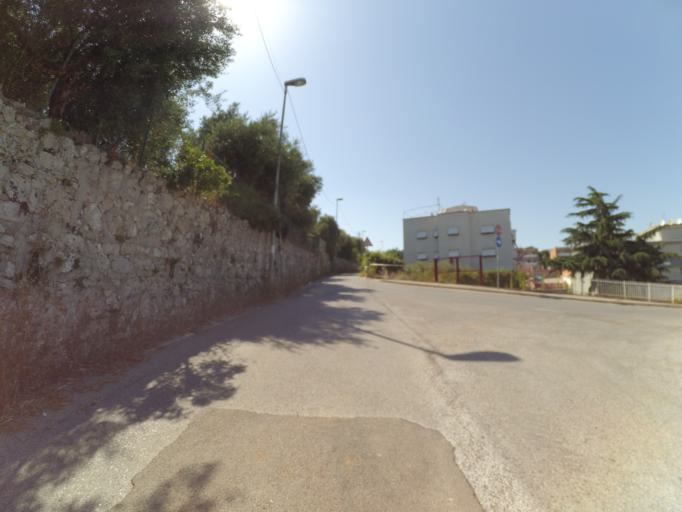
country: IT
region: Latium
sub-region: Provincia di Latina
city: Gaeta
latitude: 41.2184
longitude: 13.5568
